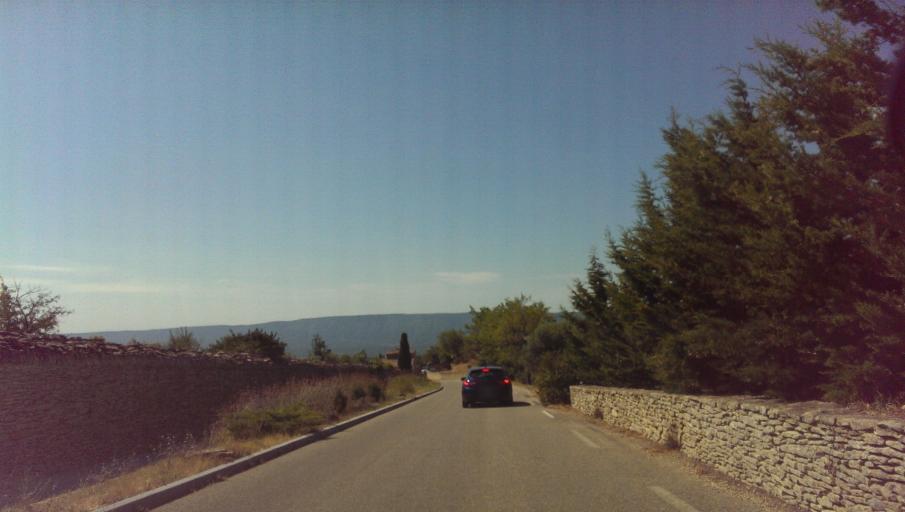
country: FR
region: Provence-Alpes-Cote d'Azur
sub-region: Departement du Vaucluse
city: Gordes
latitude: 43.9180
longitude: 5.2019
